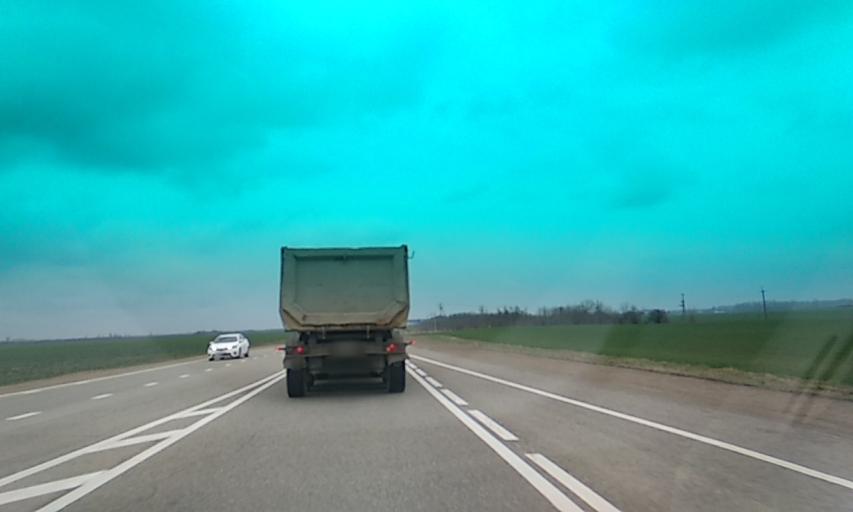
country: RU
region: Krasnodarskiy
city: Velikovechnoye
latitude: 44.9017
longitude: 39.8021
